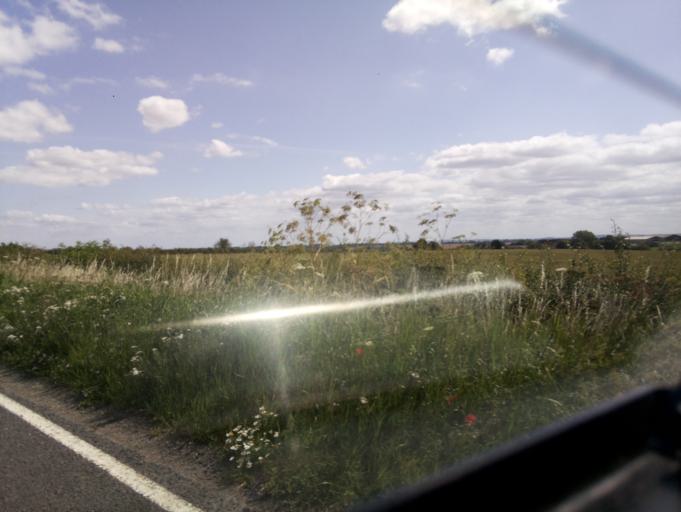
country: GB
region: England
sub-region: Buckinghamshire
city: Winslow
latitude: 51.8919
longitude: -0.8332
